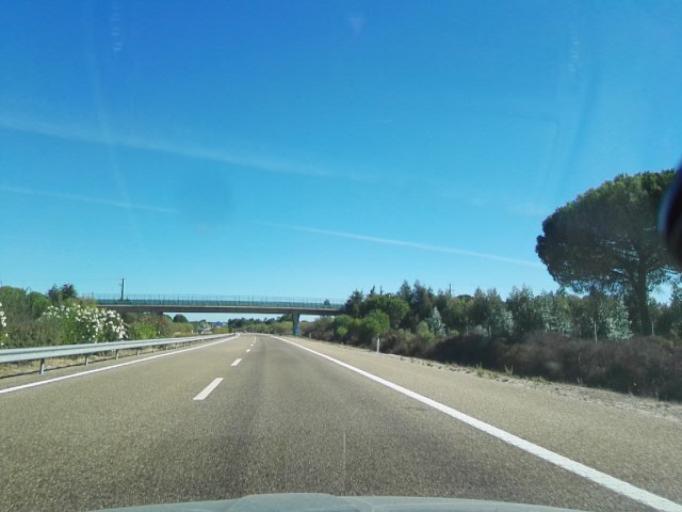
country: PT
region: Evora
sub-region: Vendas Novas
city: Vendas Novas
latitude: 38.6759
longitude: -8.6428
